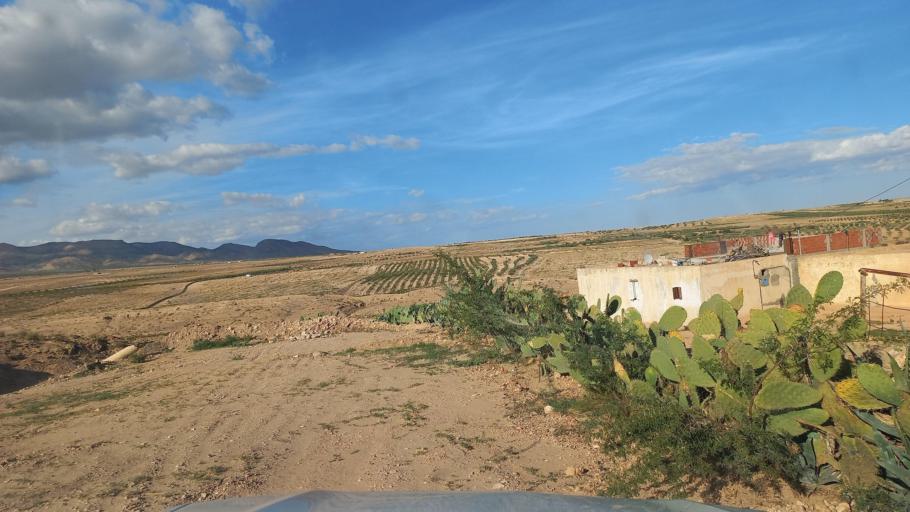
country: TN
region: Al Qasrayn
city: Sbiba
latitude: 35.3854
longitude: 9.0240
